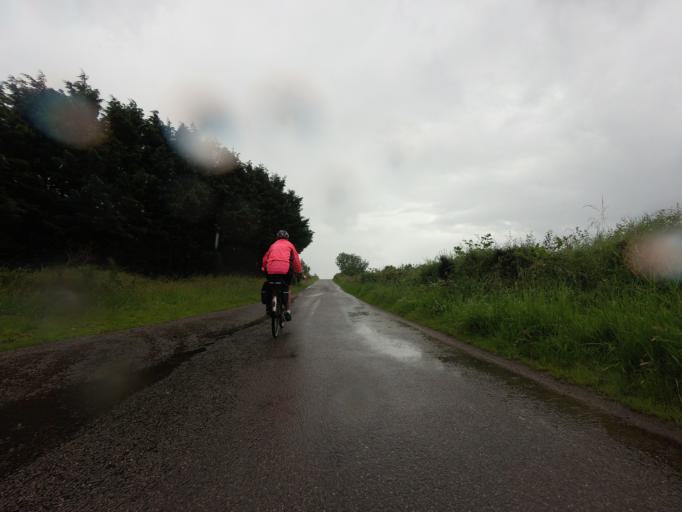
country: GB
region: Scotland
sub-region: Moray
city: Fochabers
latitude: 57.6636
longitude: -3.0731
